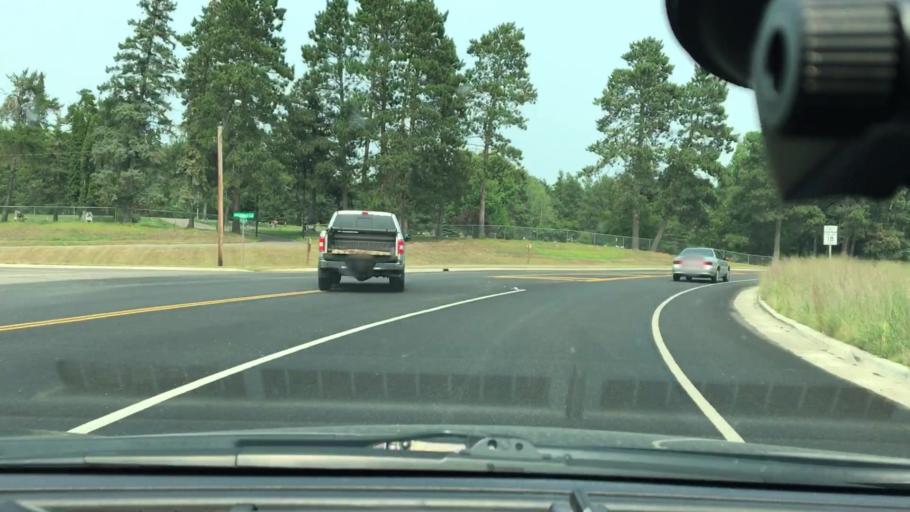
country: US
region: Minnesota
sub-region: Crow Wing County
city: Nisswa
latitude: 46.5209
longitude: -94.2803
